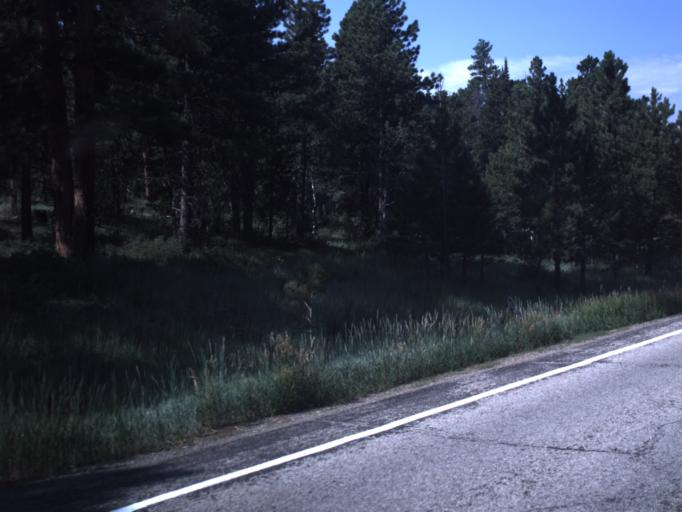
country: US
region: Utah
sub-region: Daggett County
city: Manila
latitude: 40.8614
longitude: -109.5332
